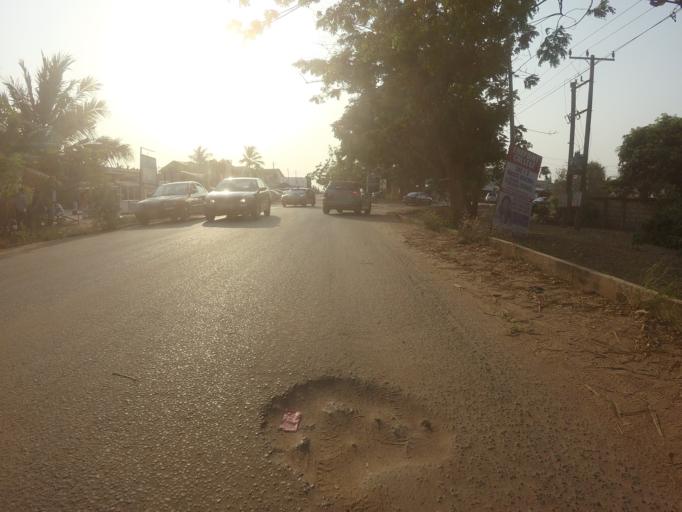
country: GH
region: Greater Accra
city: Nungua
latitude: 5.6162
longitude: -0.0515
